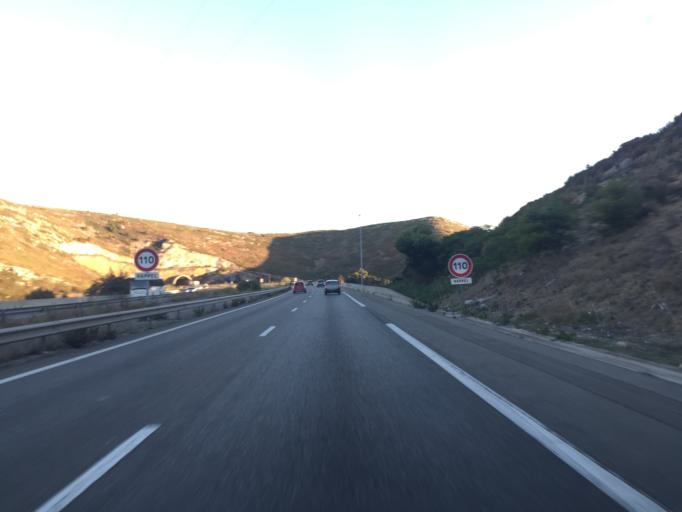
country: FR
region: Provence-Alpes-Cote d'Azur
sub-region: Departement des Bouches-du-Rhone
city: Marseille 16
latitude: 43.3734
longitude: 5.3198
